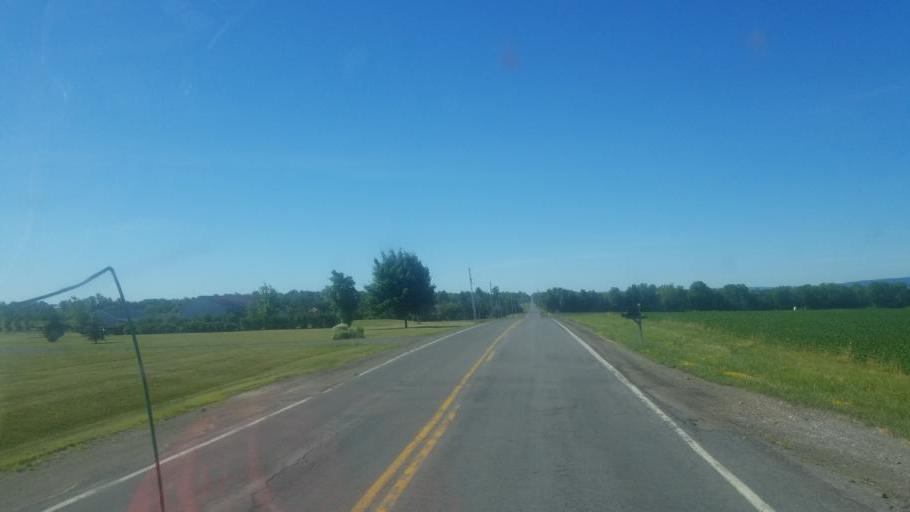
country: US
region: New York
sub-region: Ontario County
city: Canandaigua
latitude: 42.8434
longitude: -77.2306
